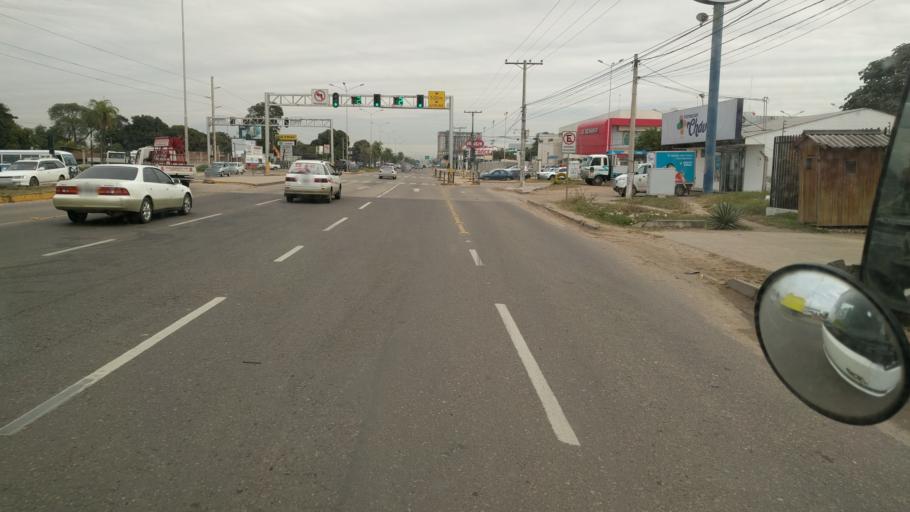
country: BO
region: Santa Cruz
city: Santa Cruz de la Sierra
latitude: -17.7156
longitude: -63.1619
